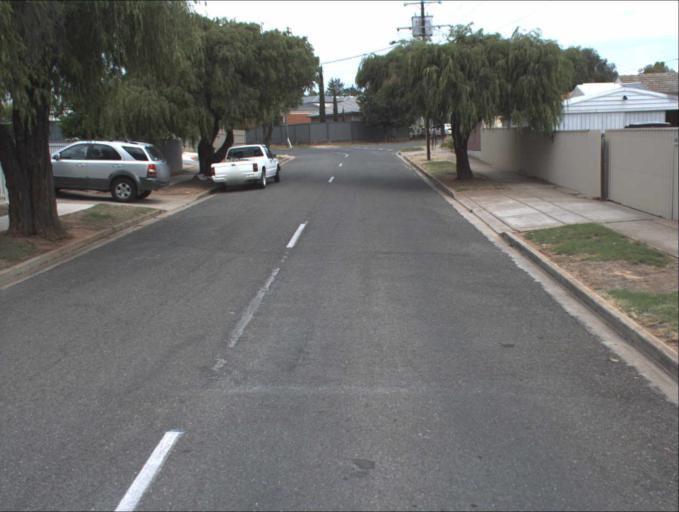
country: AU
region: South Australia
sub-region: Port Adelaide Enfield
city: Enfield
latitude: -34.8541
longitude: 138.6031
